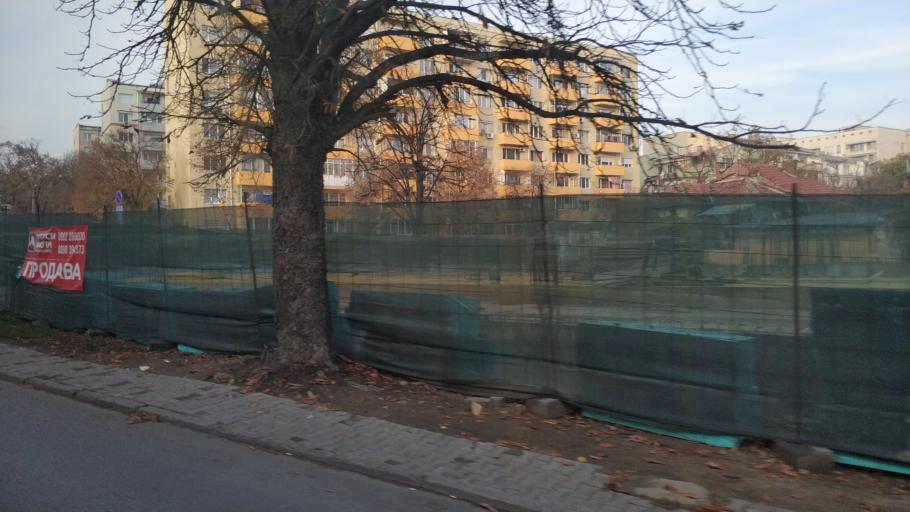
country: BG
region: Stara Zagora
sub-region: Obshtina Stara Zagora
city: Stara Zagora
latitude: 42.4199
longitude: 25.6195
